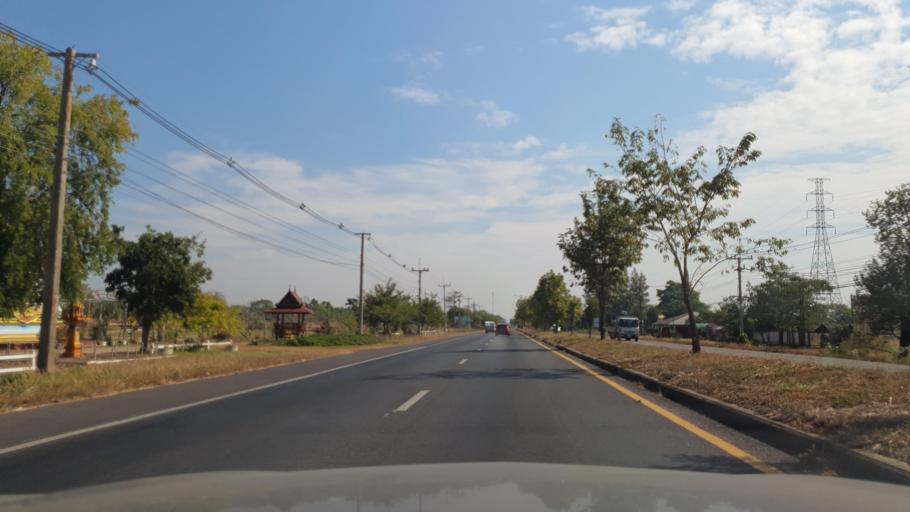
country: TH
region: Maha Sarakham
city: Kantharawichai
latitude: 16.3886
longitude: 103.2597
